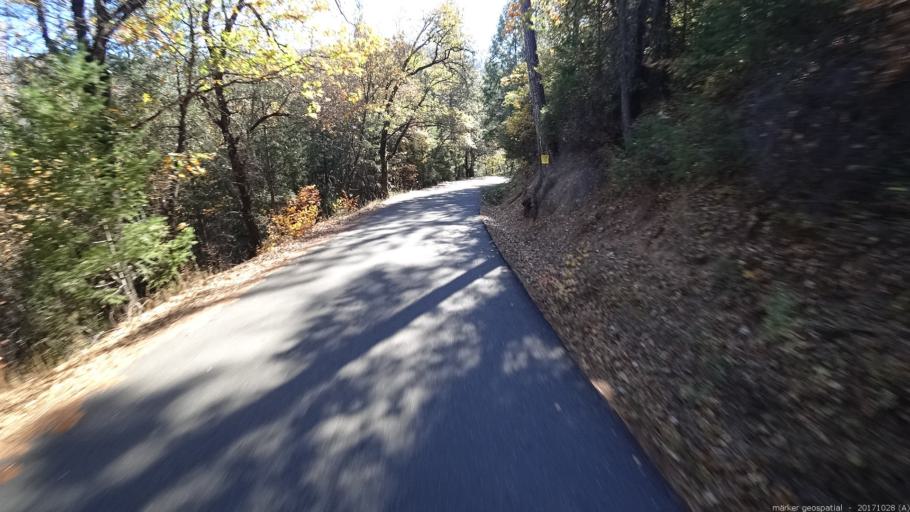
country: US
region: California
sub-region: Trinity County
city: Lewiston
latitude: 40.7972
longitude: -122.6104
